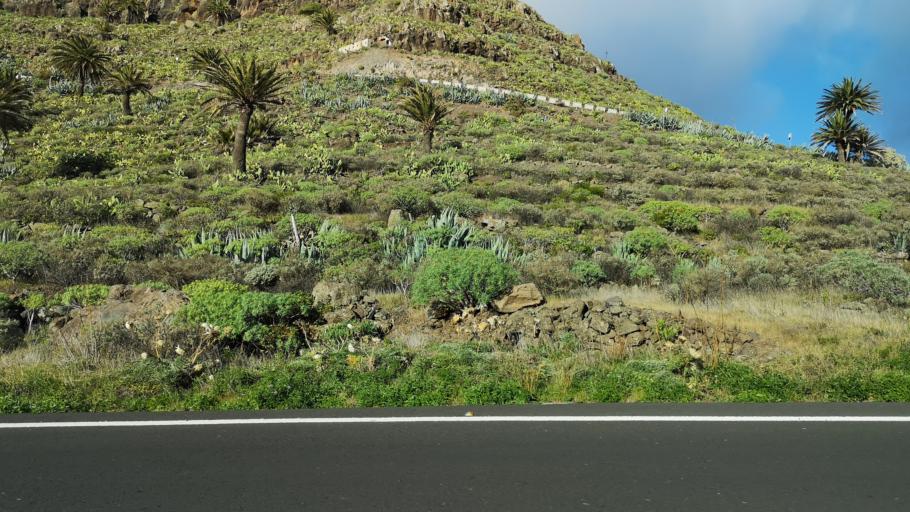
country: ES
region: Canary Islands
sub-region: Provincia de Santa Cruz de Tenerife
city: Vallehermosa
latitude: 28.1202
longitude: -17.3165
